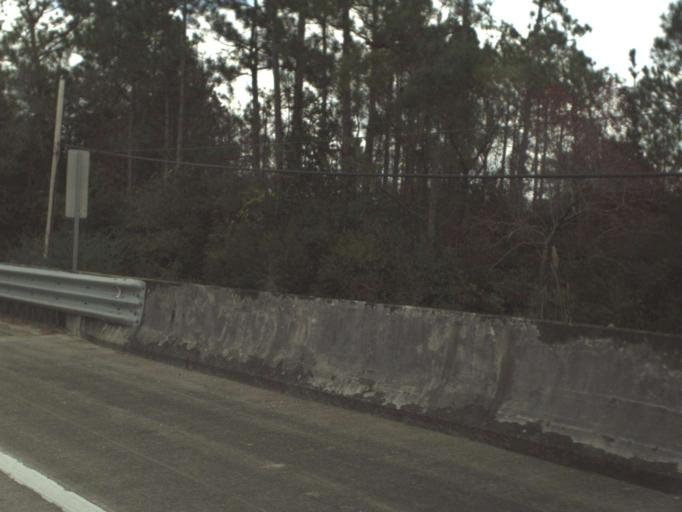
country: US
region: Florida
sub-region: Santa Rosa County
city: Point Baker
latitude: 30.7125
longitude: -87.0460
